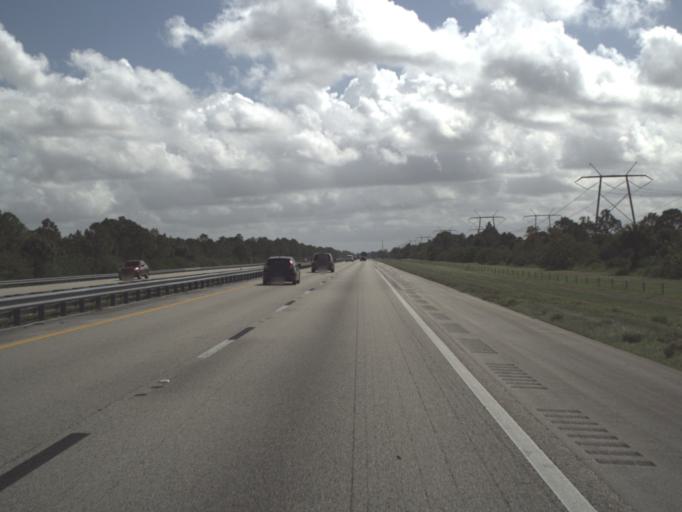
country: US
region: Florida
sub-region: Indian River County
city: West Vero Corridor
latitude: 27.5471
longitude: -80.6289
